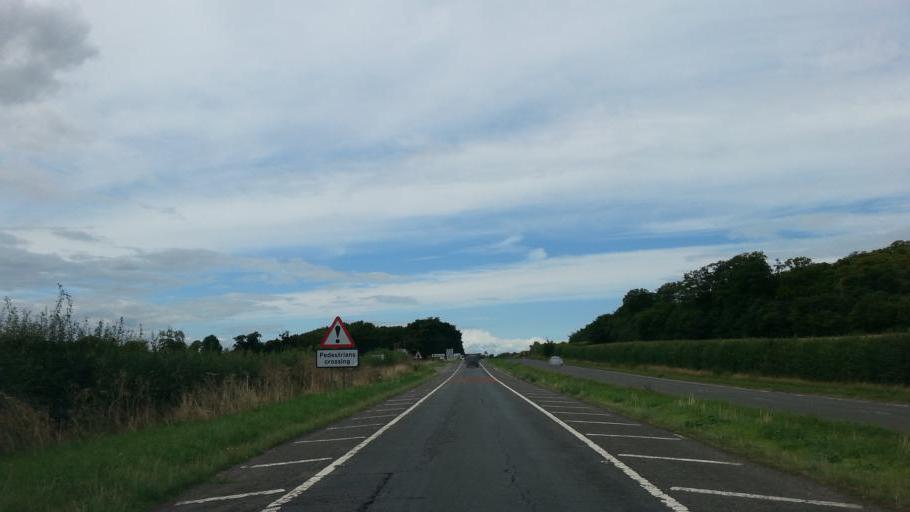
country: GB
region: England
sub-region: Cambridgeshire
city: Sawston
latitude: 52.1316
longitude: 0.2169
